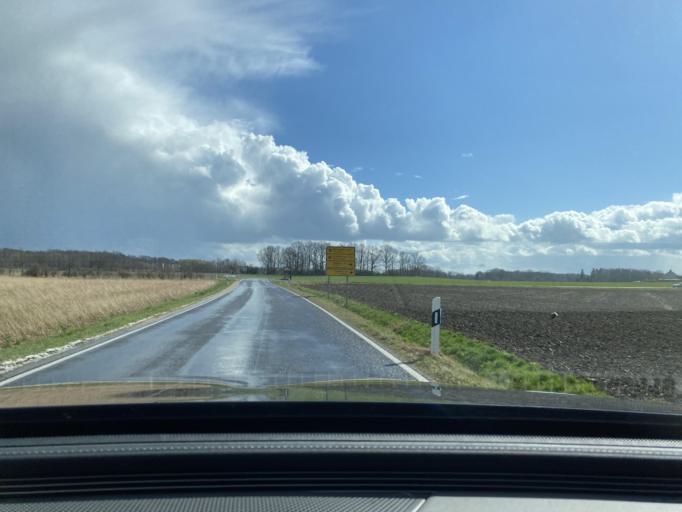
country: DE
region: Saxony
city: Radibor
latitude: 51.2577
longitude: 14.4271
